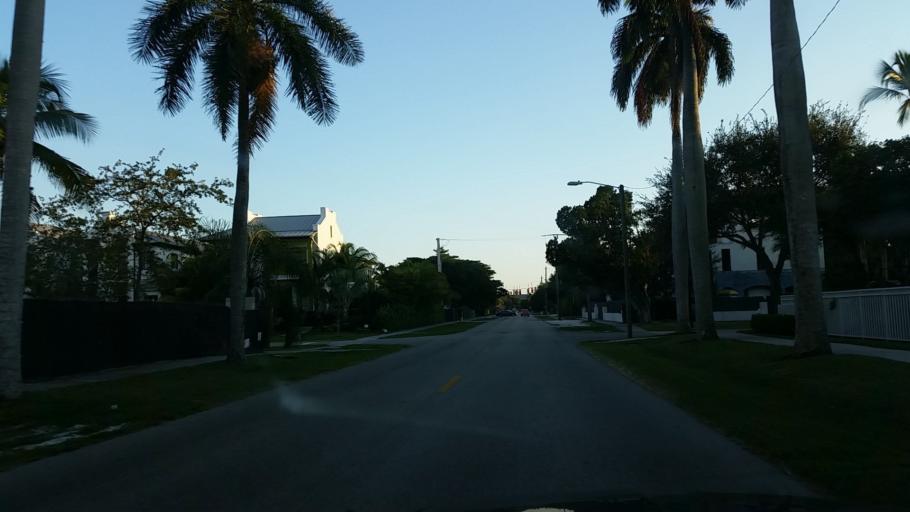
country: US
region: Florida
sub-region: Collier County
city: Naples
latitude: 26.1380
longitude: -81.7943
